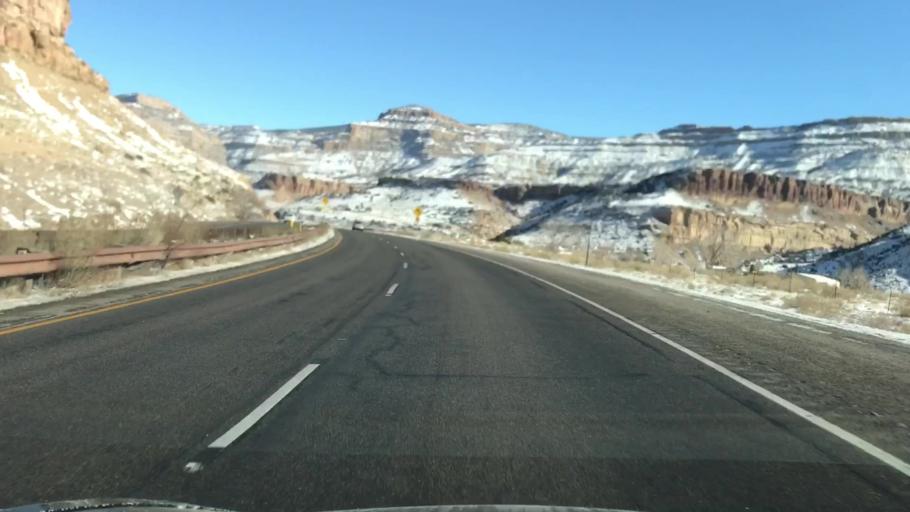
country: US
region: Colorado
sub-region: Mesa County
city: Palisade
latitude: 39.1182
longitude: -108.3286
